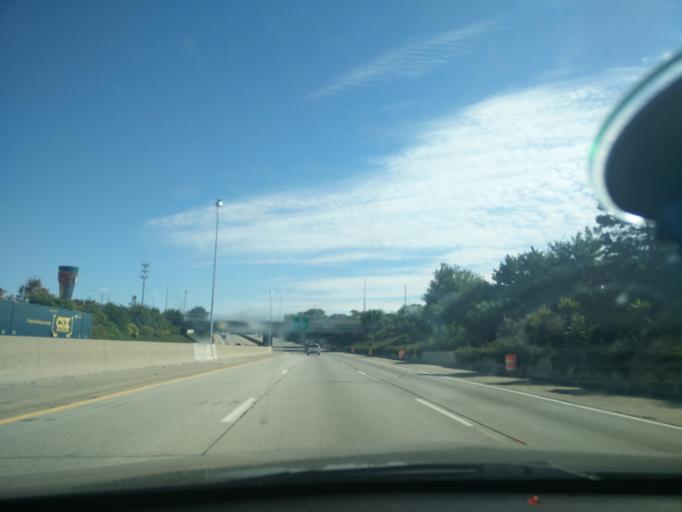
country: US
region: Michigan
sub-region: Macomb County
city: Roseville
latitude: 42.4945
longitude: -82.9409
